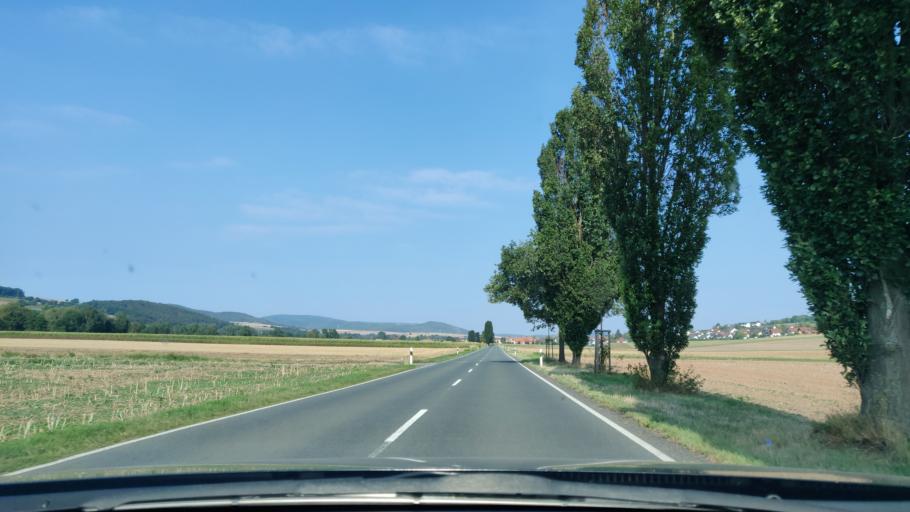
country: DE
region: Hesse
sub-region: Regierungsbezirk Kassel
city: Bad Wildungen
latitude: 51.1393
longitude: 9.1940
